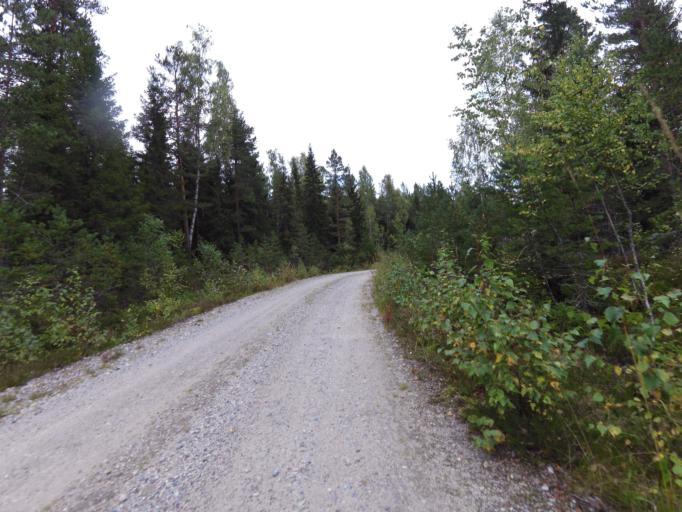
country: SE
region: Gaevleborg
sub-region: Gavle Kommun
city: Valbo
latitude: 60.7400
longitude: 17.0230
